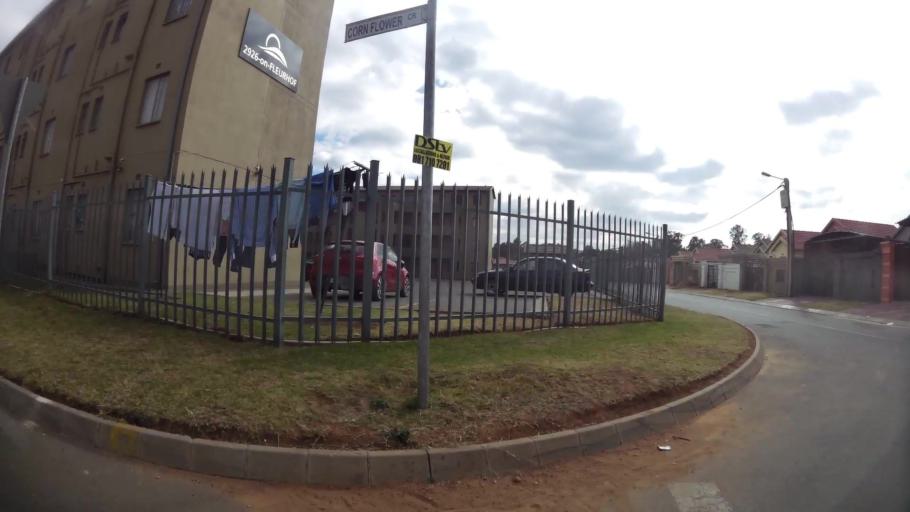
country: ZA
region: Gauteng
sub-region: City of Johannesburg Metropolitan Municipality
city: Roodepoort
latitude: -26.2047
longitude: 27.9165
